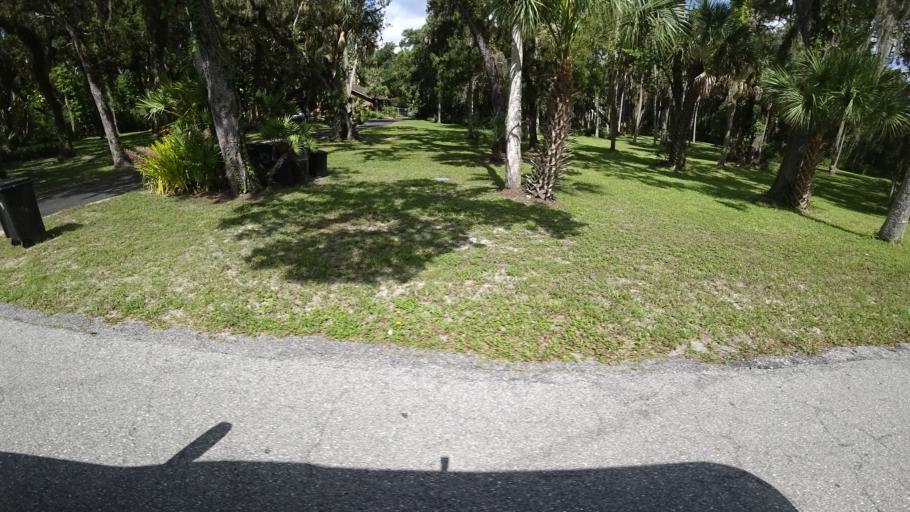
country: US
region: Florida
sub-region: Manatee County
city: Samoset
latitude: 27.4645
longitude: -82.4784
